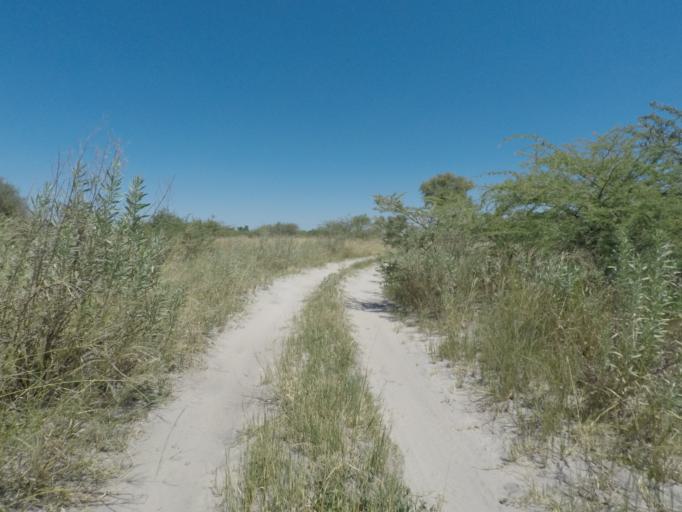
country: BW
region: North West
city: Maun
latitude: -19.4446
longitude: 23.5589
